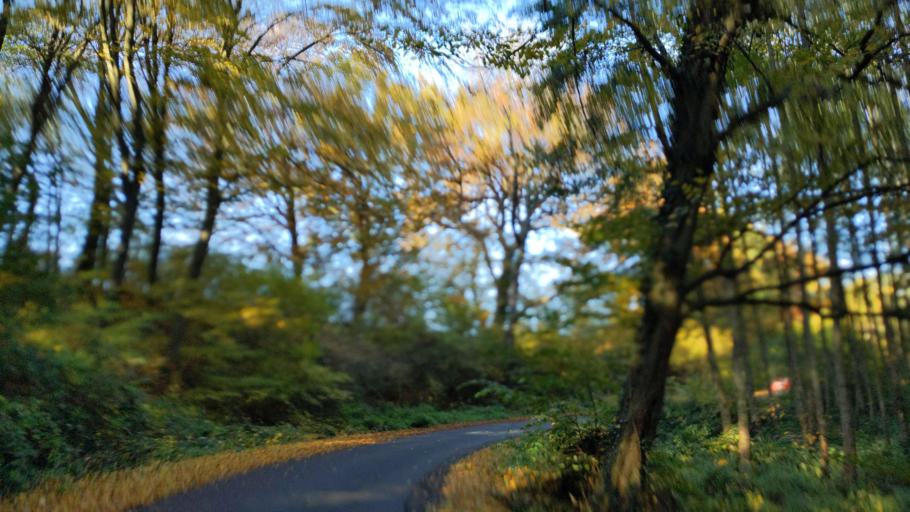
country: DE
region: Schleswig-Holstein
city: Kasseedorf
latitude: 54.1393
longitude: 10.7018
